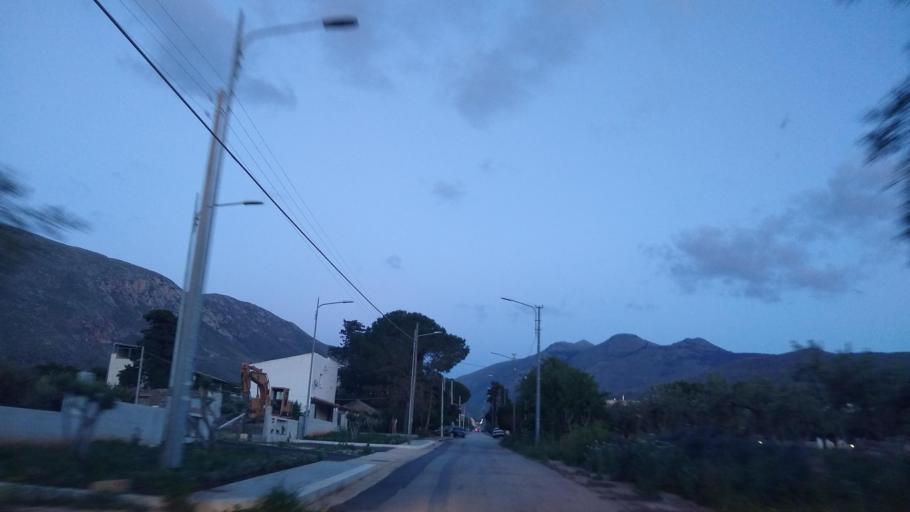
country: IT
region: Sicily
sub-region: Trapani
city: Castelluzzo
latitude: 38.1053
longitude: 12.7308
